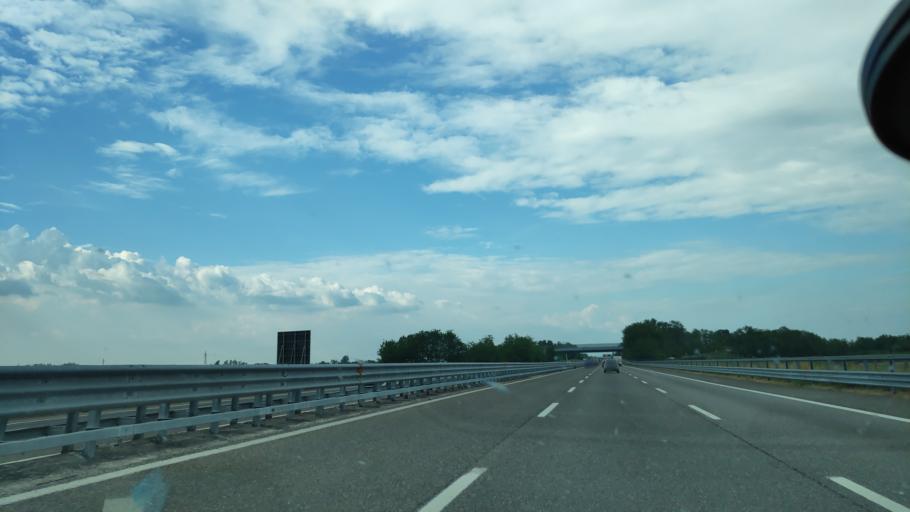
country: IT
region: Lombardy
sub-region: Provincia di Pavia
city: Gropello Cairoli
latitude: 45.1536
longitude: 8.9945
